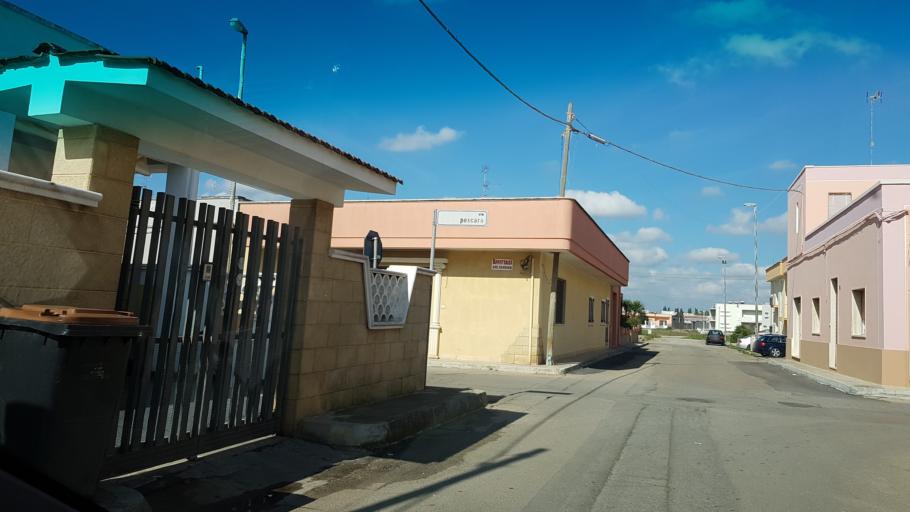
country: IT
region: Apulia
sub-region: Provincia di Lecce
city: Veglie
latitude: 40.3392
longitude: 17.9605
